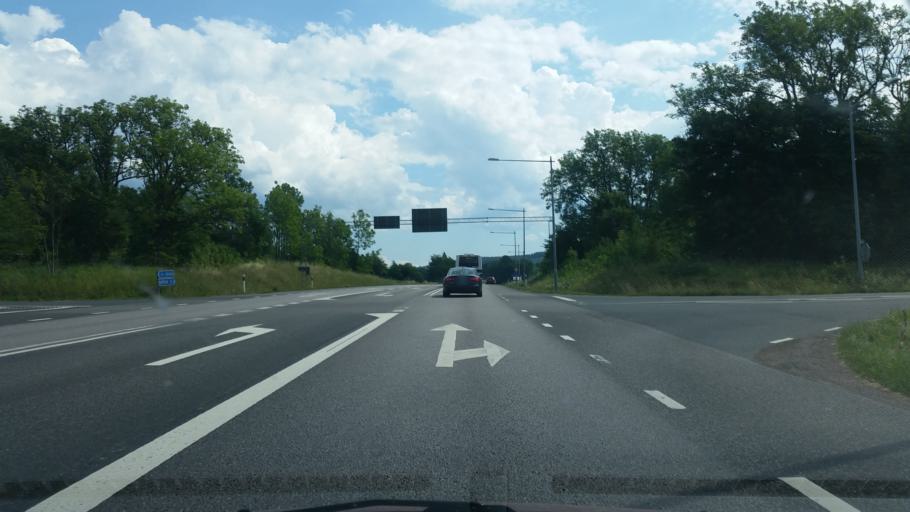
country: SE
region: Vaestra Goetaland
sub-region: Skara Kommun
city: Axvall
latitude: 58.3899
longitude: 13.6503
